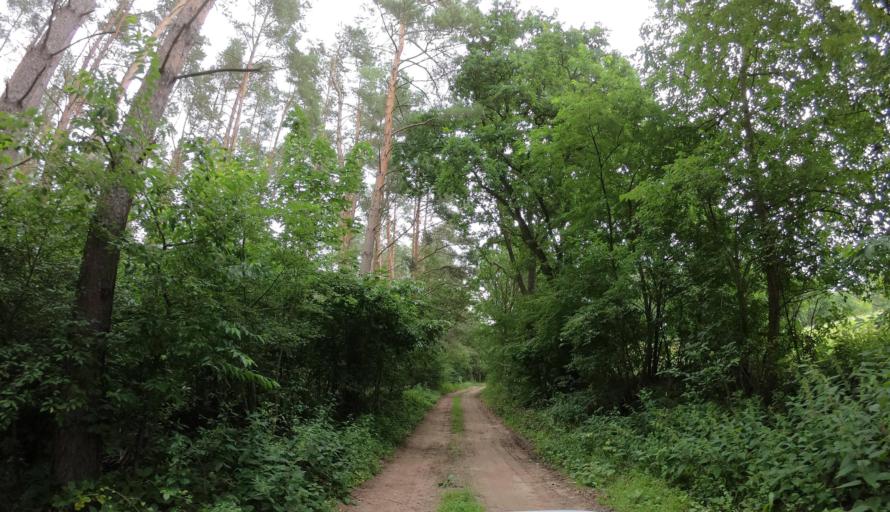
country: PL
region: West Pomeranian Voivodeship
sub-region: Powiat goleniowski
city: Przybiernow
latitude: 53.8258
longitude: 14.7442
